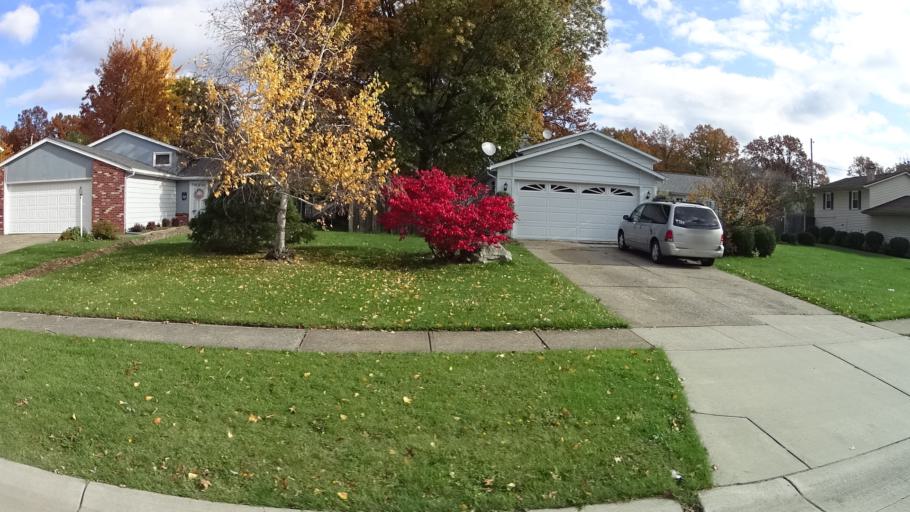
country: US
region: Ohio
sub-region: Lorain County
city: Lorain
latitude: 41.4232
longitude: -82.1993
